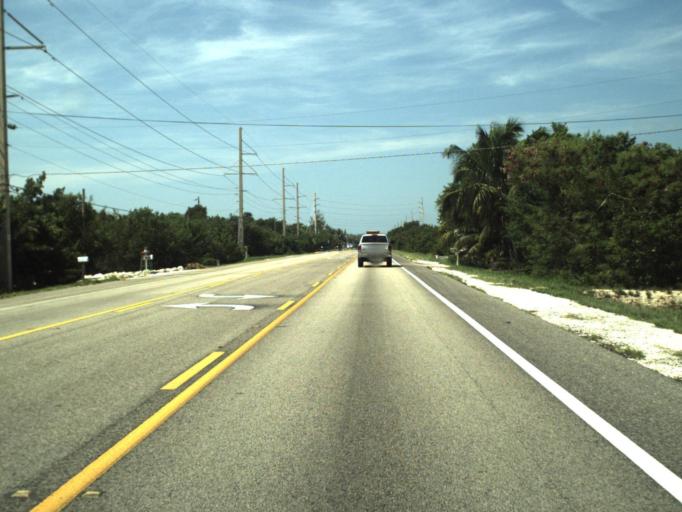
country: US
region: Florida
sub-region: Monroe County
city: Marathon
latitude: 24.7639
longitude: -80.9490
